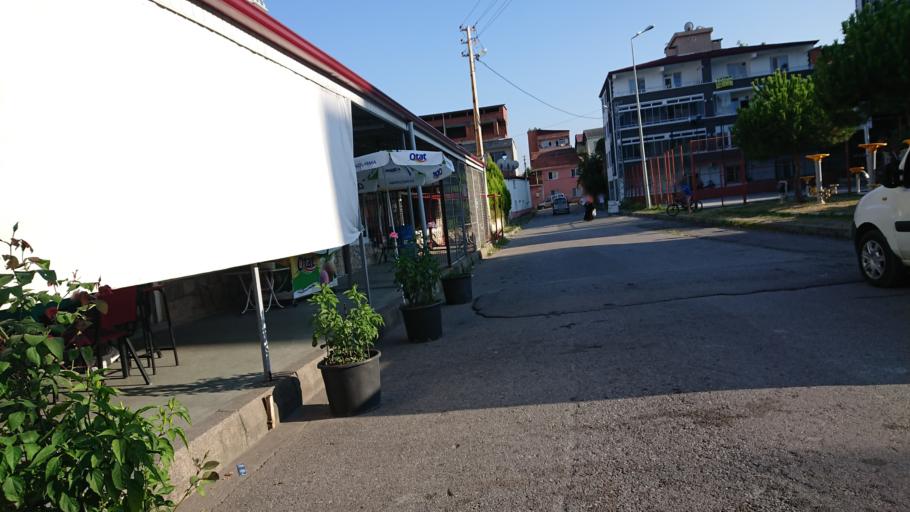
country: TR
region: Samsun
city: Samsun
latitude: 41.2990
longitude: 36.3208
